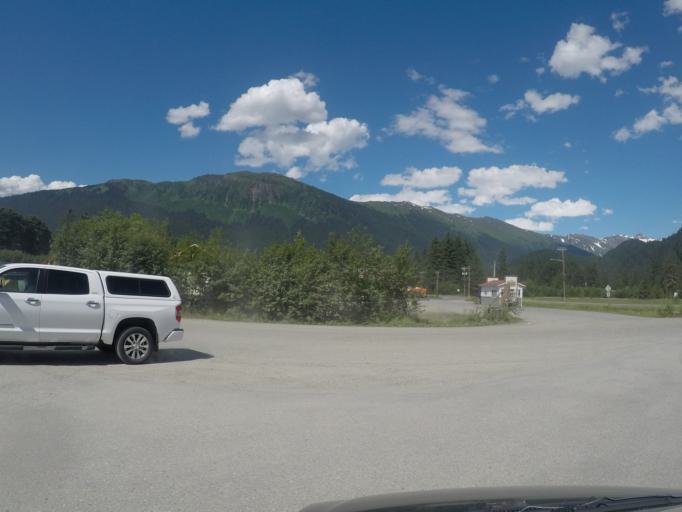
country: US
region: Alaska
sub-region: Juneau City and Borough
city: Juneau
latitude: 58.3513
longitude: -134.4922
